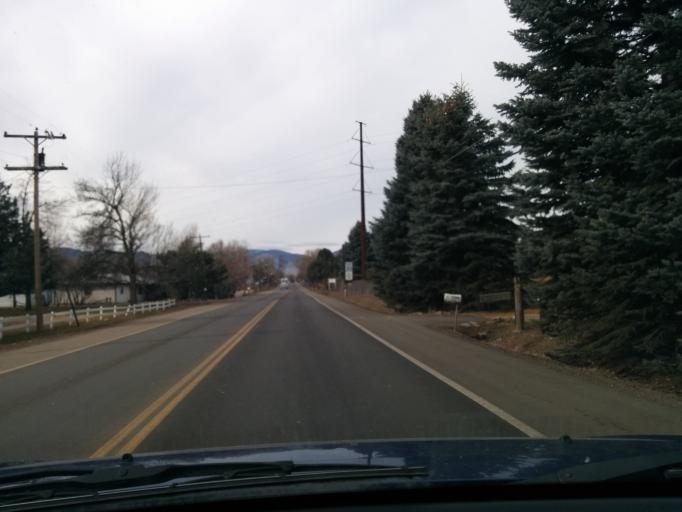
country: US
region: Colorado
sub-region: Larimer County
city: Fort Collins
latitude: 40.5965
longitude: -105.1064
